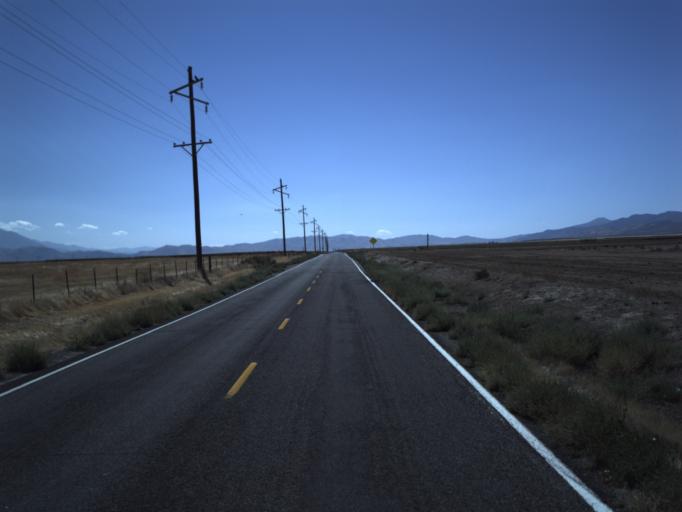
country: US
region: Utah
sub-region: Utah County
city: Genola
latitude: 40.1152
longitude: -111.9592
